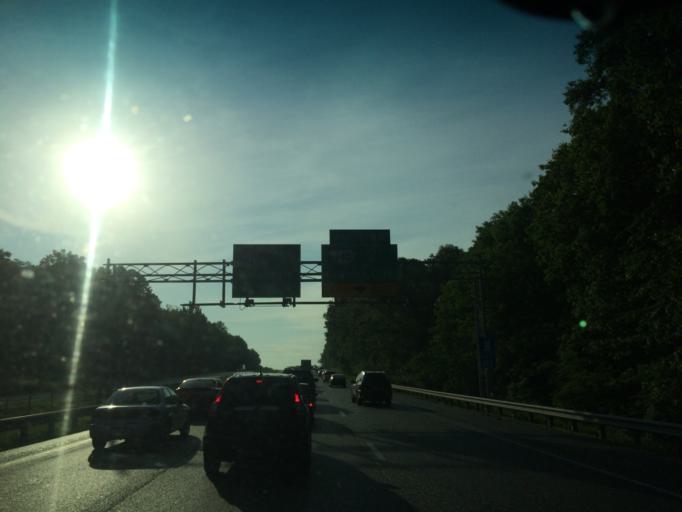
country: US
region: Maryland
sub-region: Carroll County
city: Sykesville
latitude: 39.3058
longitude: -76.9252
